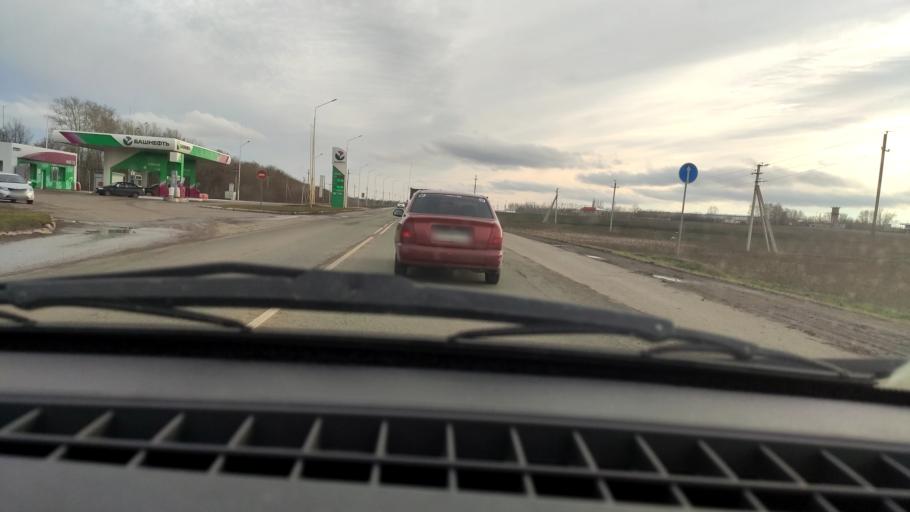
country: RU
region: Bashkortostan
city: Chishmy
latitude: 54.5729
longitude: 55.3563
